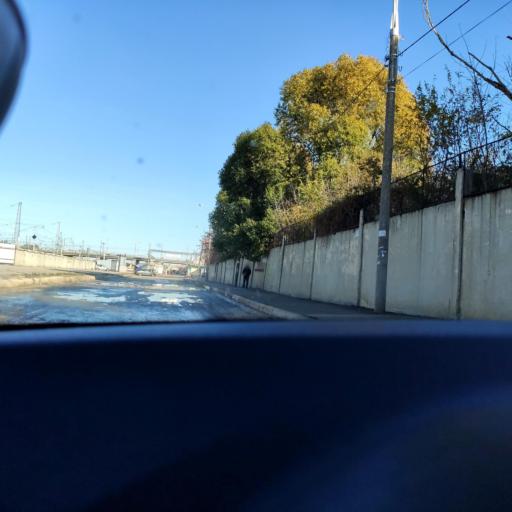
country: RU
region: Samara
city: Samara
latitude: 53.2108
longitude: 50.2661
